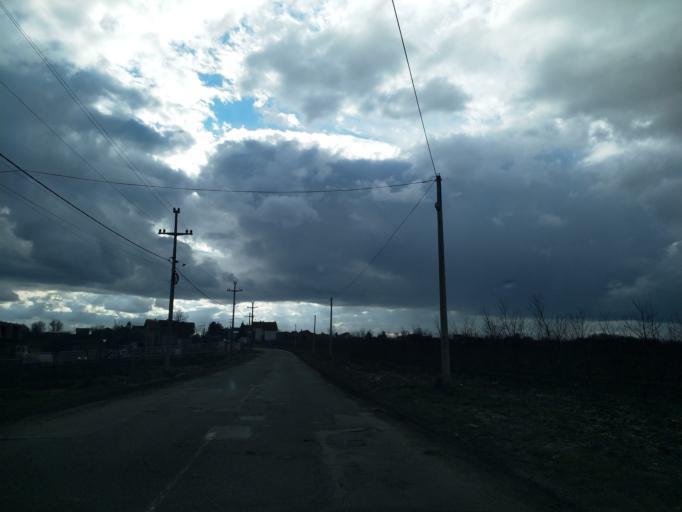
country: RS
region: Central Serbia
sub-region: Belgrade
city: Grocka
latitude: 44.6186
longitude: 20.7323
